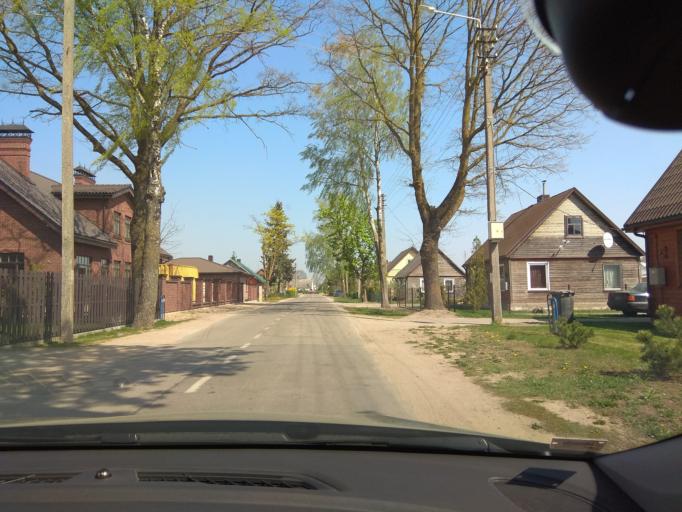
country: LT
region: Siauliu apskritis
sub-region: Joniskis
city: Joniskis
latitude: 56.2476
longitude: 23.6159
